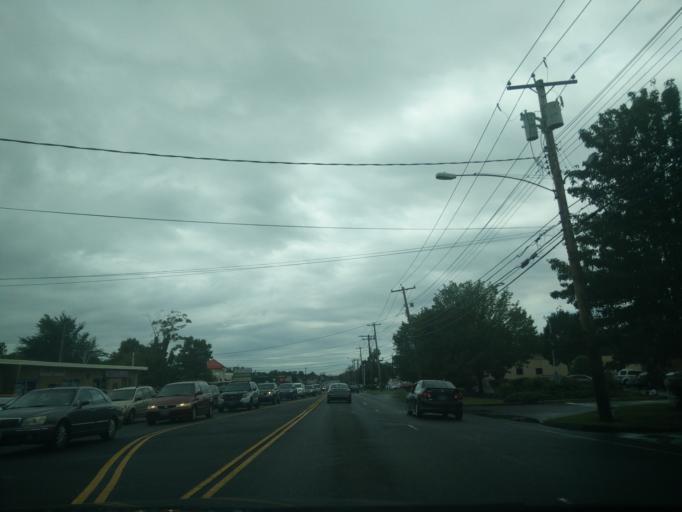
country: US
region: Connecticut
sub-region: New Haven County
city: Orange
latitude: 41.2675
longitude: -73.0007
